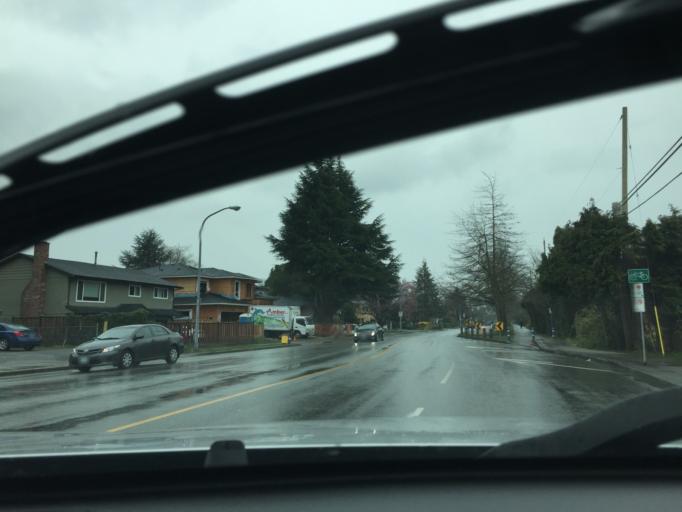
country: CA
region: British Columbia
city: Richmond
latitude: 49.1481
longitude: -123.1253
